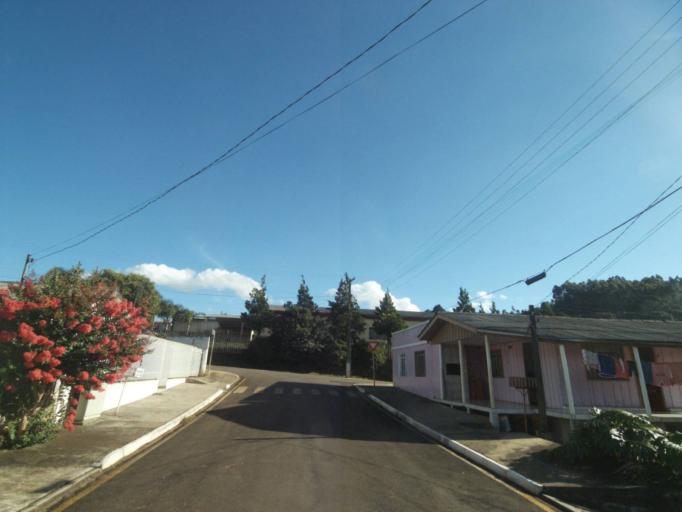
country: BR
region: Parana
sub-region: Uniao Da Vitoria
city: Uniao da Vitoria
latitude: -26.1606
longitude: -51.5380
